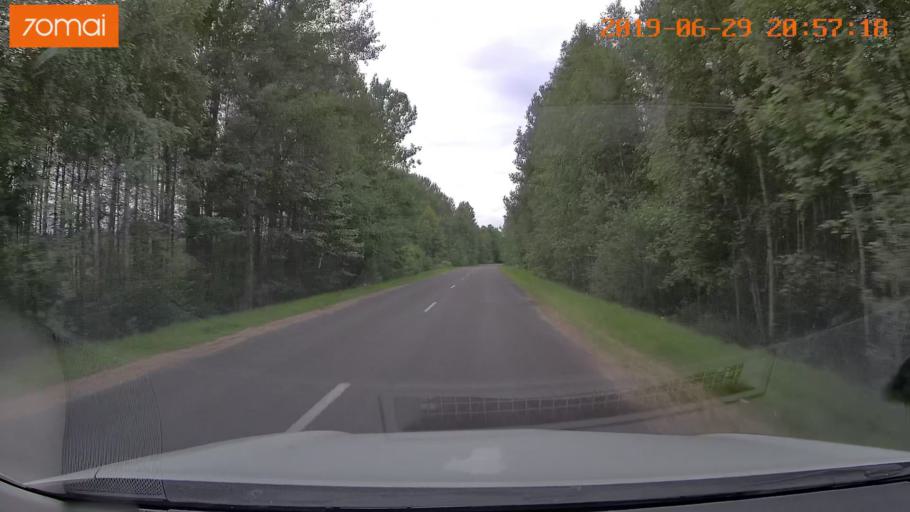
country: BY
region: Brest
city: Hantsavichy
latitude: 52.7171
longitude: 26.3699
